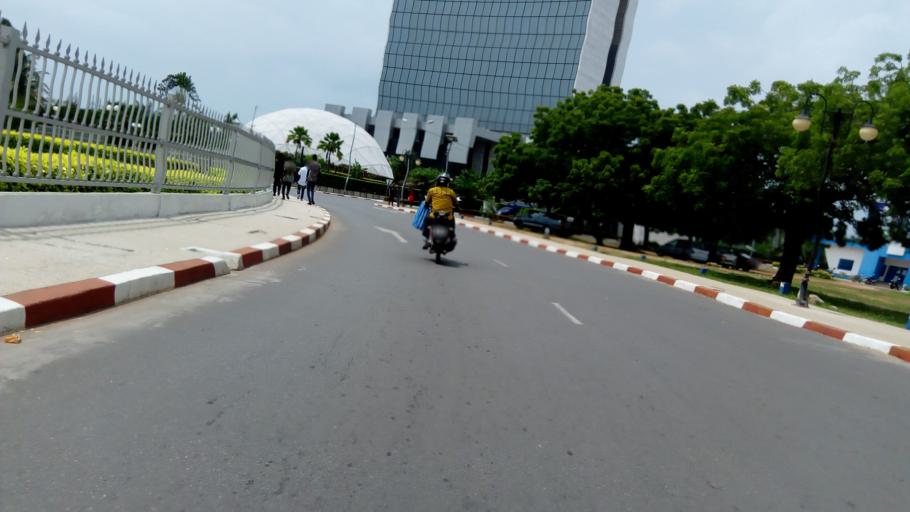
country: TG
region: Maritime
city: Lome
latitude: 6.1301
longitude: 1.2152
